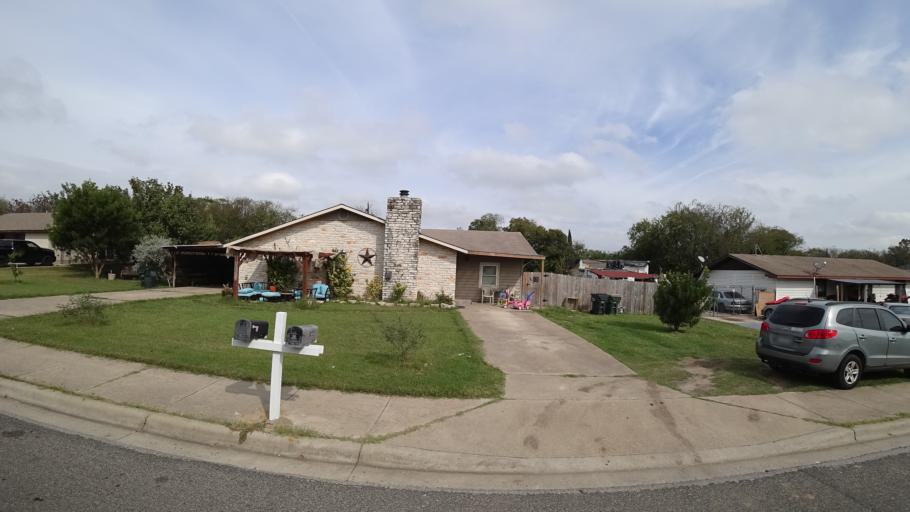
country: US
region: Texas
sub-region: Travis County
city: Wells Branch
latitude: 30.4424
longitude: -97.6607
